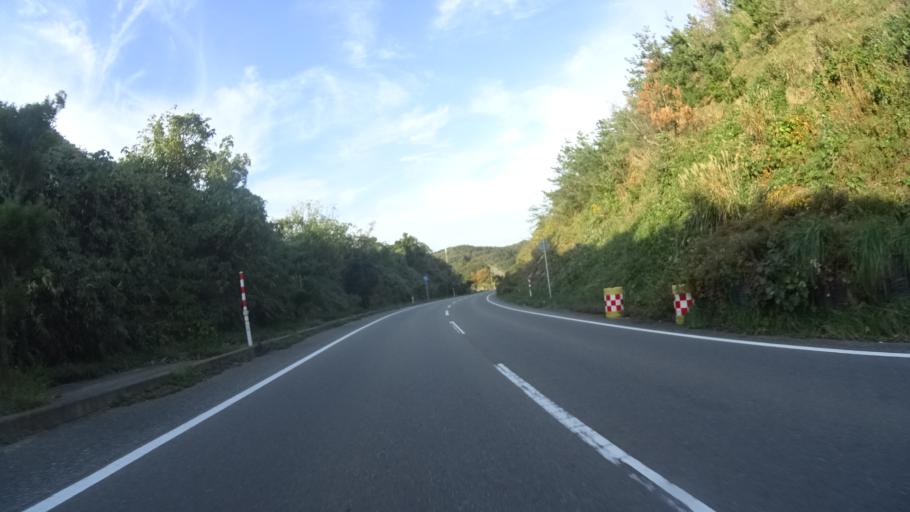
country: JP
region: Ishikawa
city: Hakui
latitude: 37.1134
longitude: 136.7278
